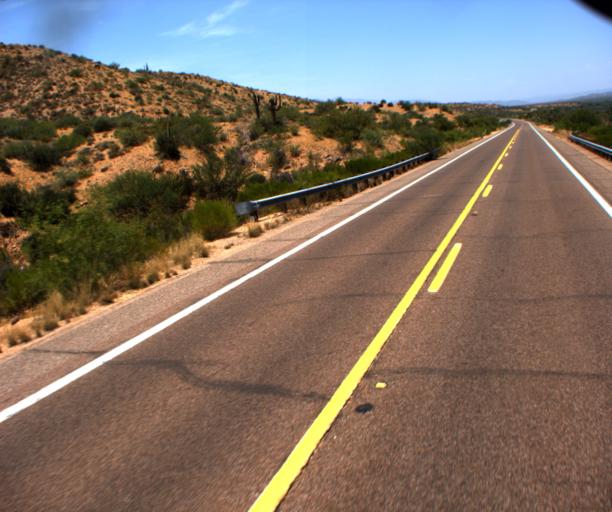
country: US
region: Arizona
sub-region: Gila County
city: Tonto Basin
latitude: 33.7690
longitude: -111.2593
